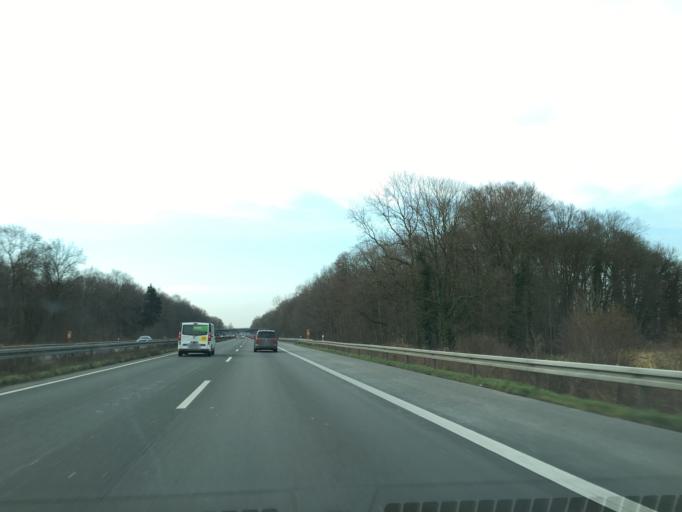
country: DE
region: North Rhine-Westphalia
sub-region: Regierungsbezirk Munster
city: Ascheberg
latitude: 51.8257
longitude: 7.6052
